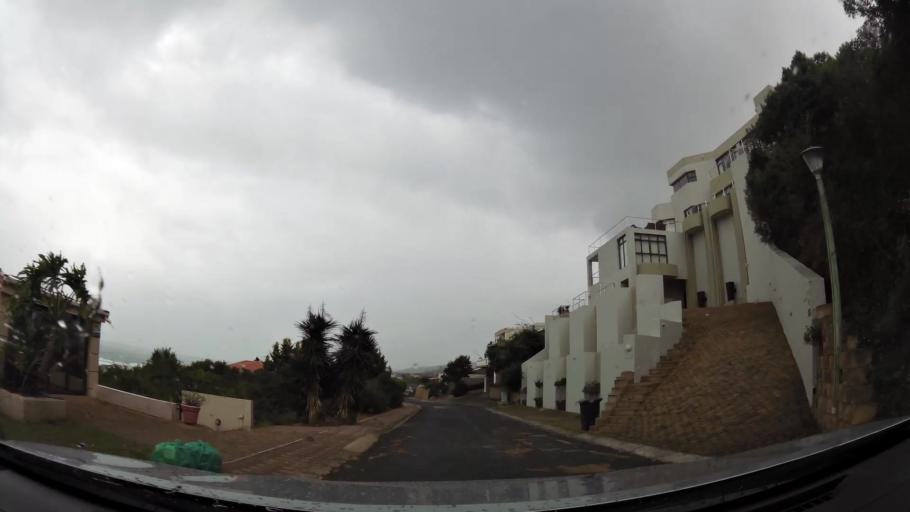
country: ZA
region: Western Cape
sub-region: Eden District Municipality
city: George
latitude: -34.0477
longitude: 22.2912
